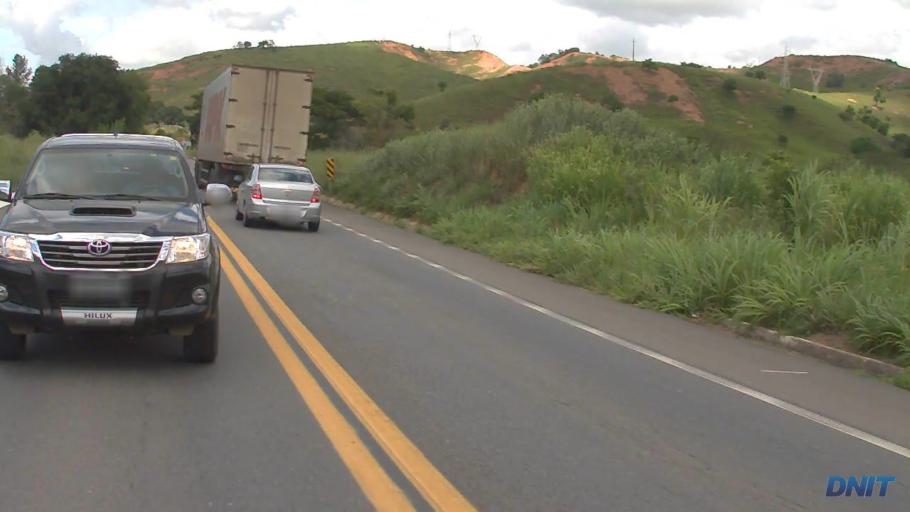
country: BR
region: Minas Gerais
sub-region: Governador Valadares
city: Governador Valadares
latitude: -18.9606
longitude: -42.0757
